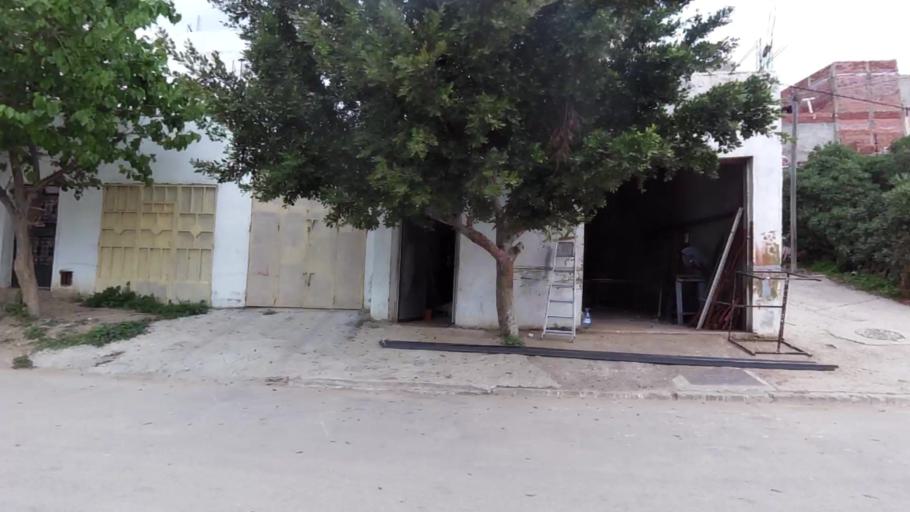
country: MA
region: Tanger-Tetouan
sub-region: Tanger-Assilah
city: Tangier
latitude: 35.7679
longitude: -5.7546
